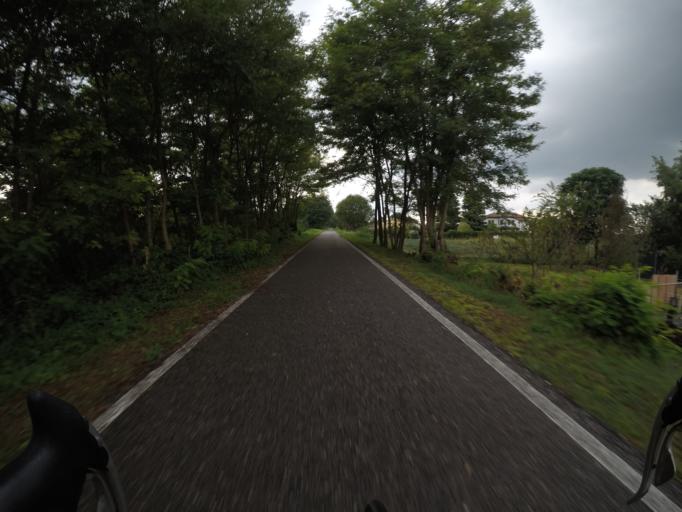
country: IT
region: Veneto
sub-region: Provincia di Rovigo
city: Frassinelle Polesine
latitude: 44.9999
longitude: 11.6899
